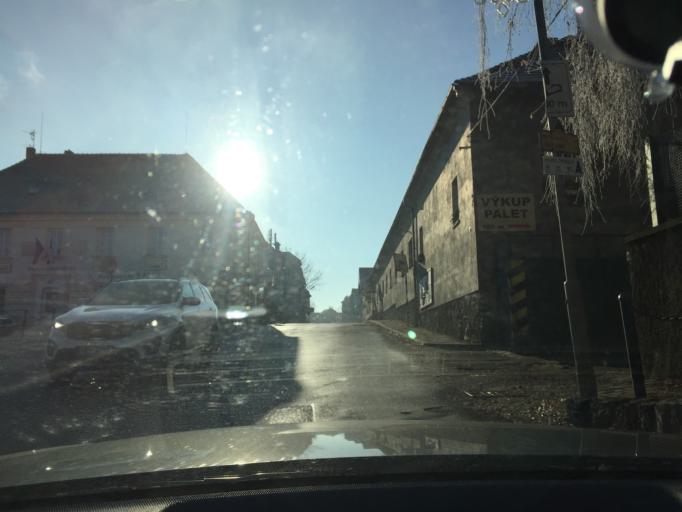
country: CZ
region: Central Bohemia
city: Trebotov
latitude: 50.0213
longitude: 14.2968
